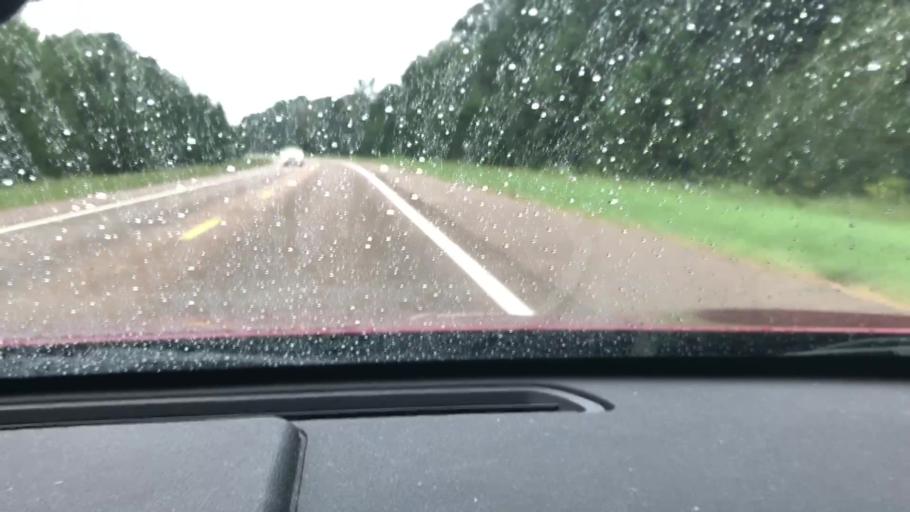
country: US
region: Arkansas
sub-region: Columbia County
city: Magnolia
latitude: 33.3002
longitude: -93.2660
